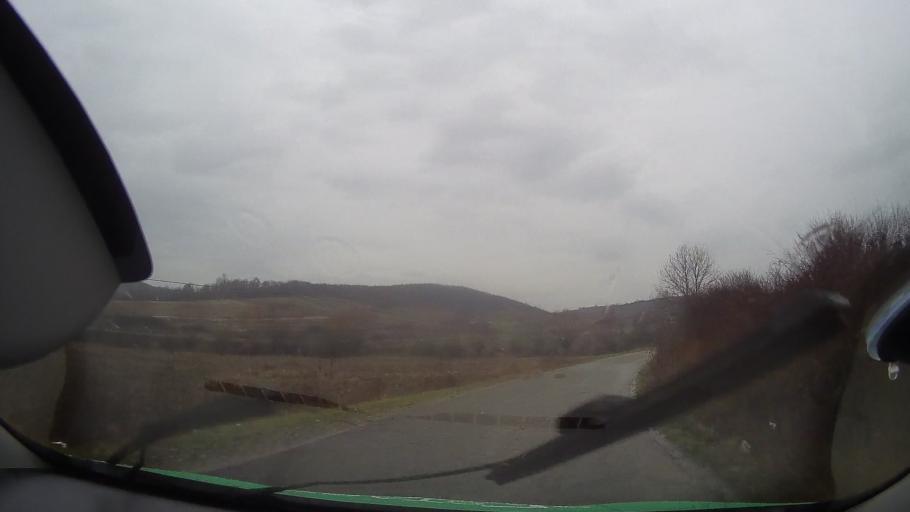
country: RO
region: Bihor
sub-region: Comuna Uileacu de Beius
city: Uileacu de Beius
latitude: 46.6900
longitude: 22.2180
